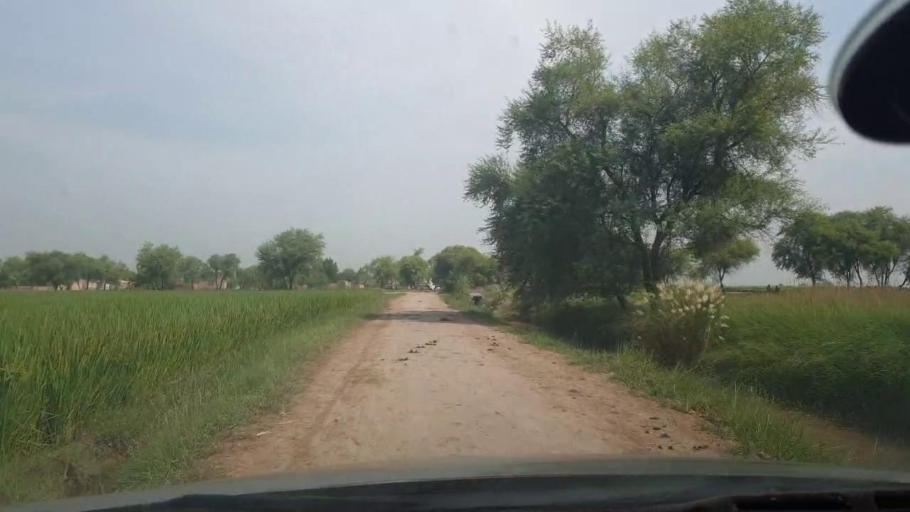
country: PK
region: Sindh
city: Jacobabad
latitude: 28.2947
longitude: 68.4803
